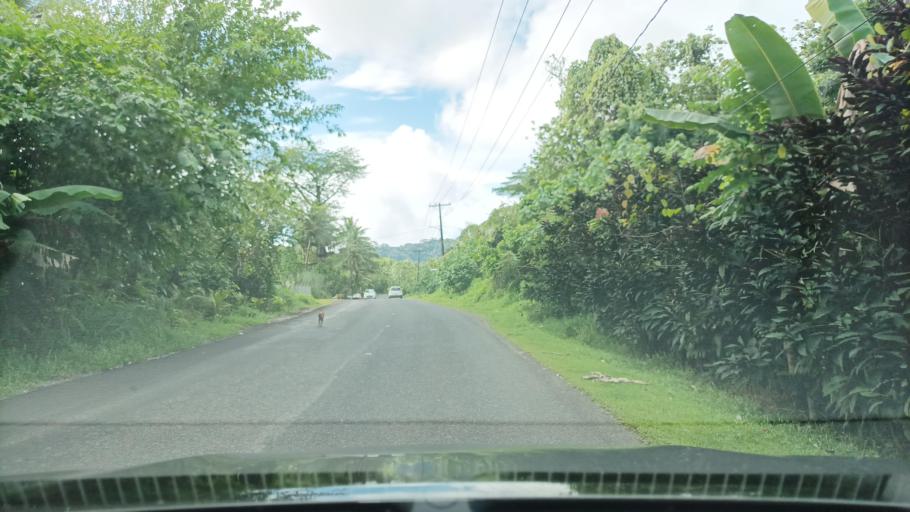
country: FM
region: Pohnpei
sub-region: Sokehs Municipality
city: Palikir - National Government Center
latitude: 6.9121
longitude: 158.1613
